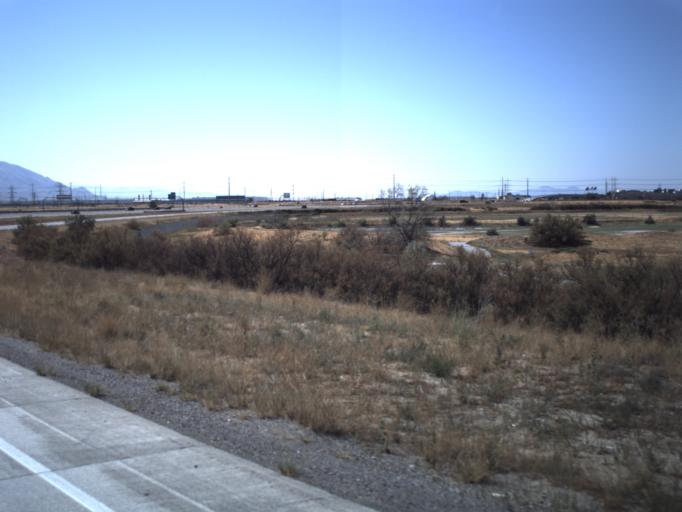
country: US
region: Utah
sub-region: Salt Lake County
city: West Valley City
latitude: 40.7667
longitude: -111.9887
